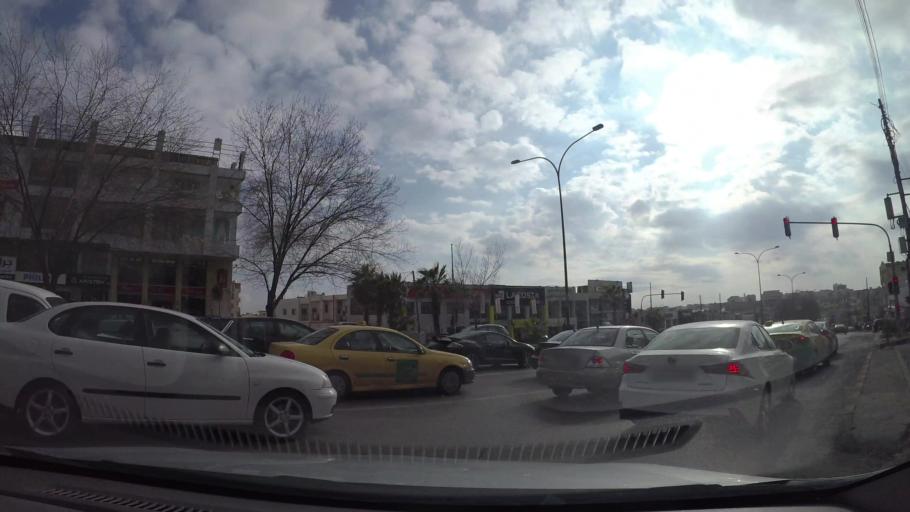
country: JO
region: Amman
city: Wadi as Sir
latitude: 31.9752
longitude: 35.8446
